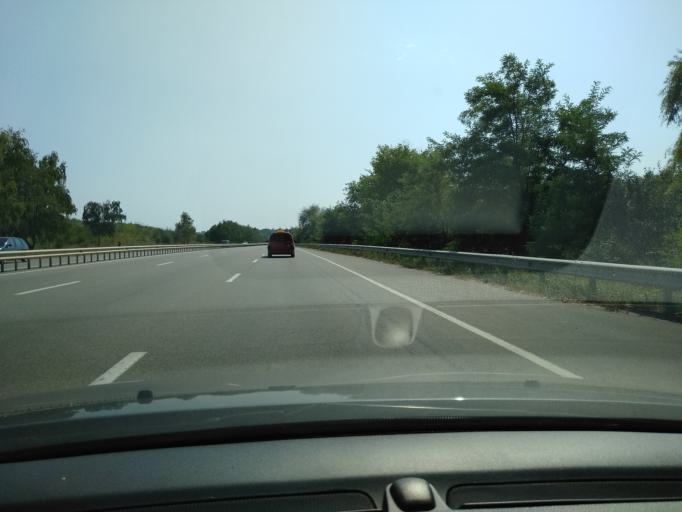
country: MD
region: Chisinau
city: Cricova
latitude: 47.1282
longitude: 28.8472
